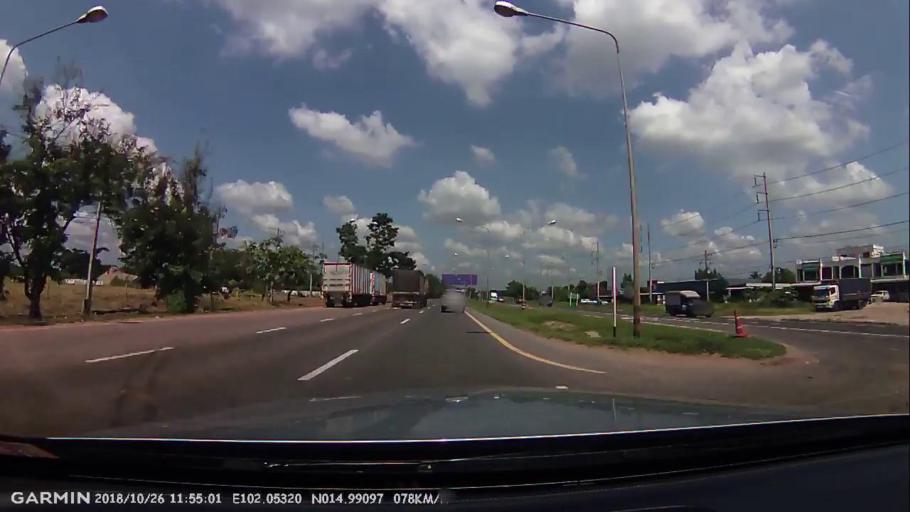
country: TH
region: Nakhon Ratchasima
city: Nakhon Ratchasima
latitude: 14.9912
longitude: 102.0532
